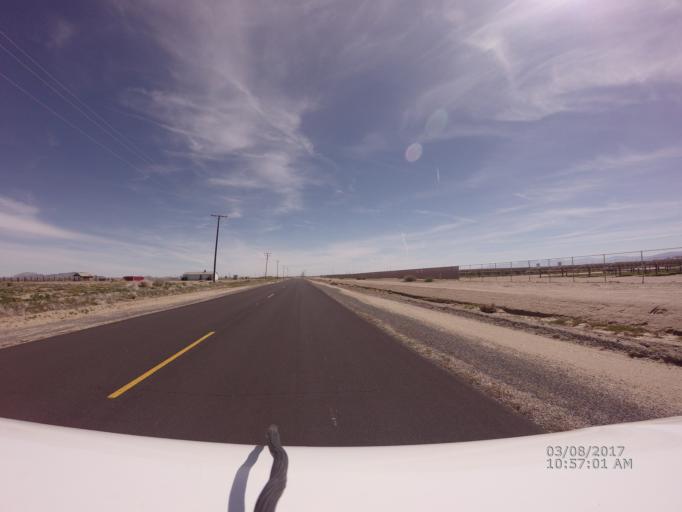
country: US
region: California
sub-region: Los Angeles County
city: Green Valley
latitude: 34.8193
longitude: -118.3655
